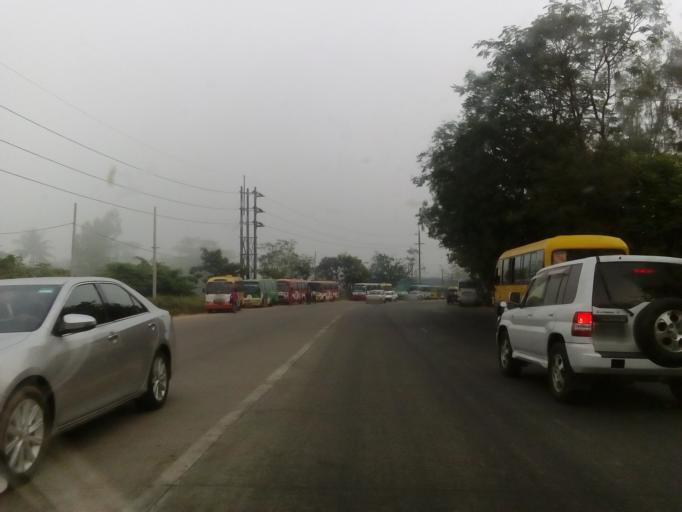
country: MM
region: Yangon
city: Yangon
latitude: 16.8100
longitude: 96.1837
